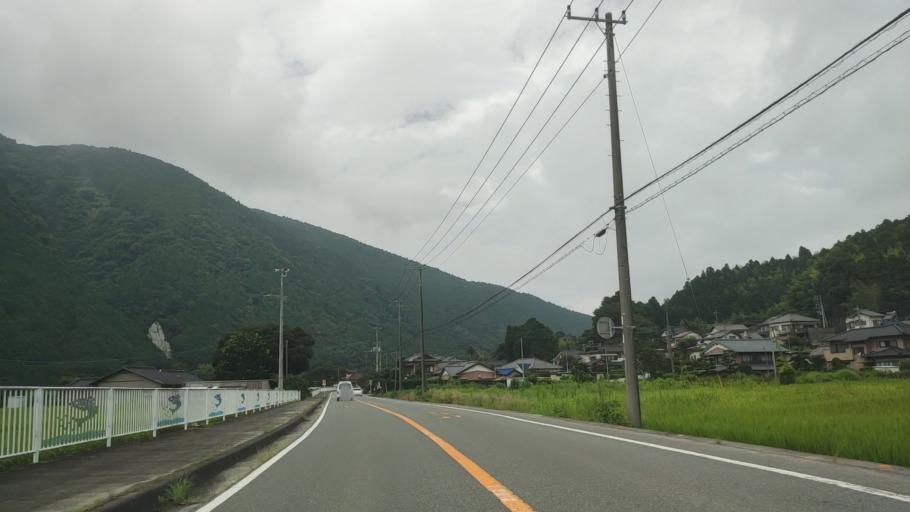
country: JP
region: Shizuoka
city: Fujinomiya
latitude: 35.2107
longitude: 138.5479
